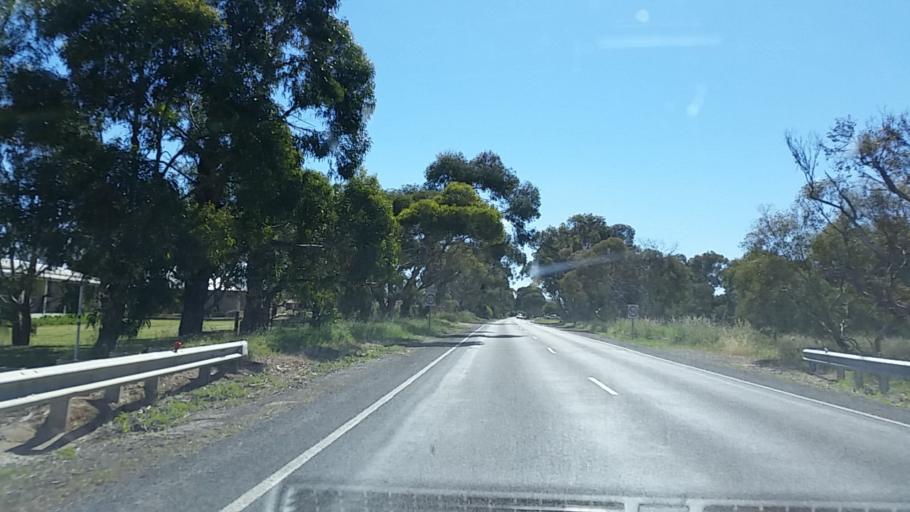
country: AU
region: South Australia
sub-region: Alexandrina
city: Strathalbyn
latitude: -35.2628
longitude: 138.9098
